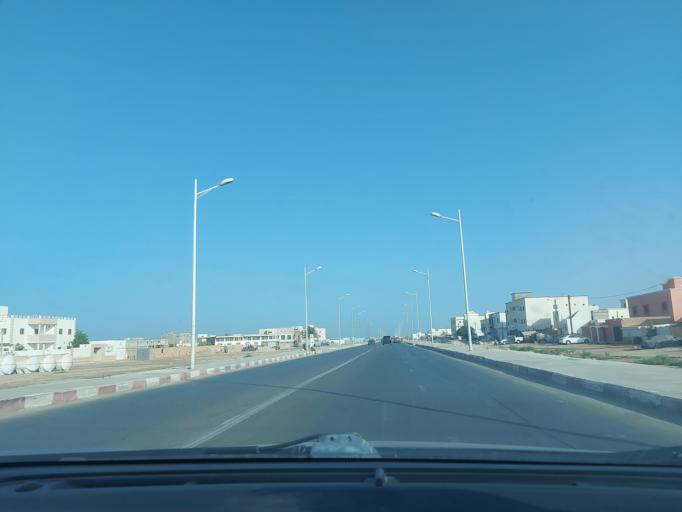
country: MR
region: Nouakchott
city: Nouakchott
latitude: 18.0930
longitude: -16.0125
